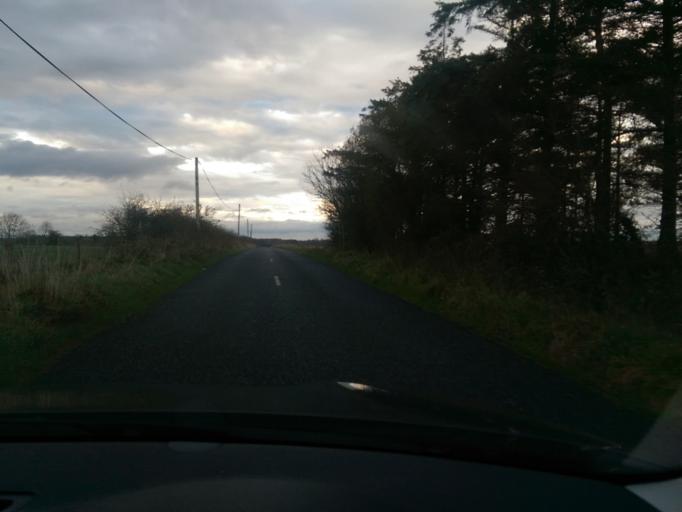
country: IE
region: Connaught
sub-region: County Galway
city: Athenry
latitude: 53.4396
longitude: -8.5633
